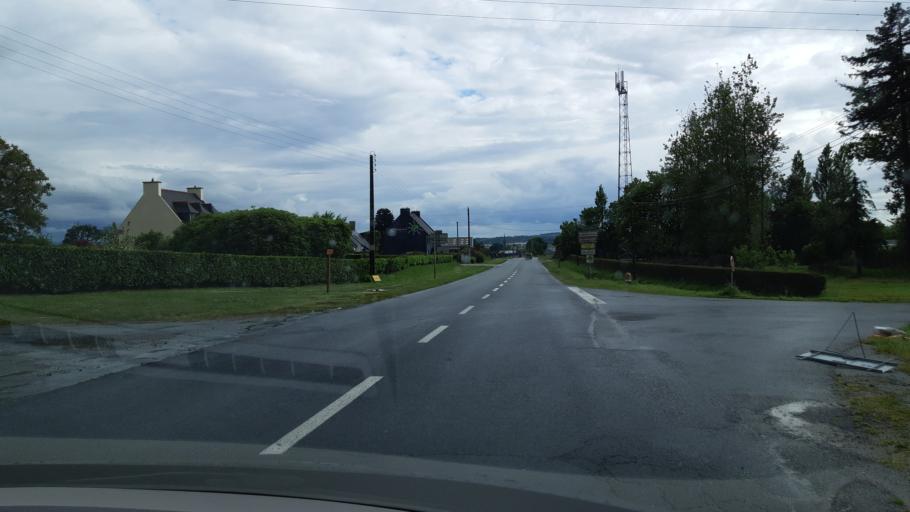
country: FR
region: Brittany
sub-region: Departement du Finistere
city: Landivisiau
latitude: 48.5256
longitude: -4.0685
